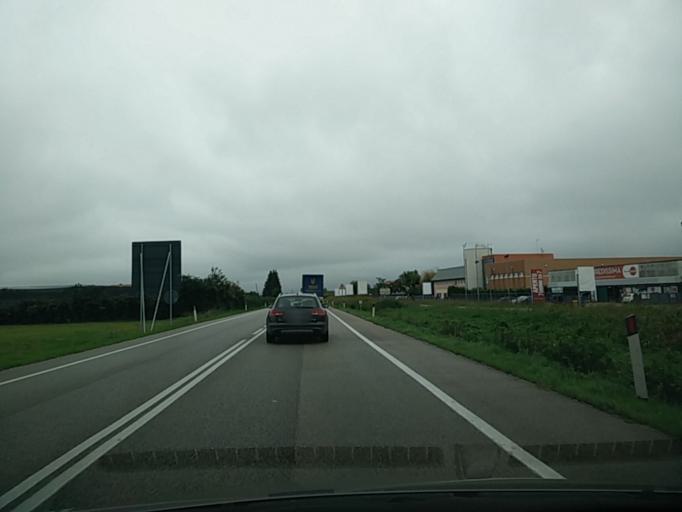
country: IT
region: Veneto
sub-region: Provincia di Treviso
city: Salvatronda
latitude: 45.6845
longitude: 11.9738
